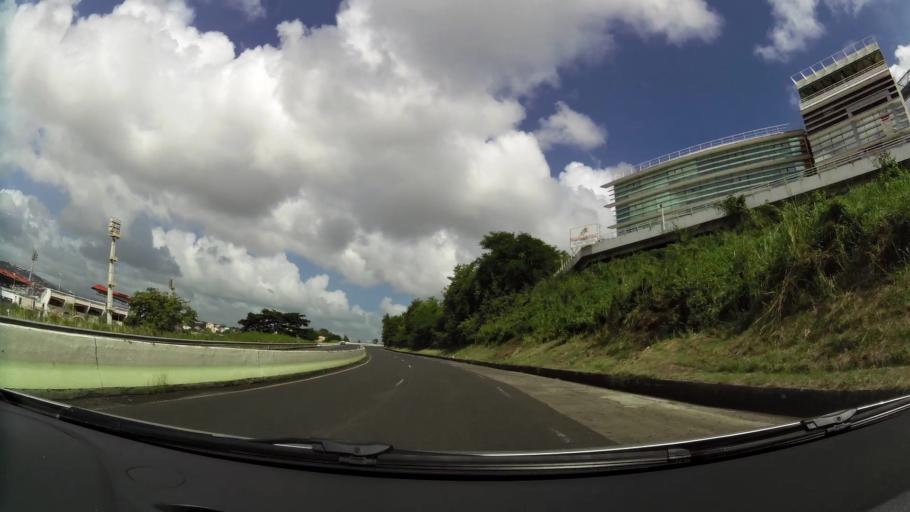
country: MQ
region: Martinique
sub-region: Martinique
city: Fort-de-France
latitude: 14.6006
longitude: -61.0457
